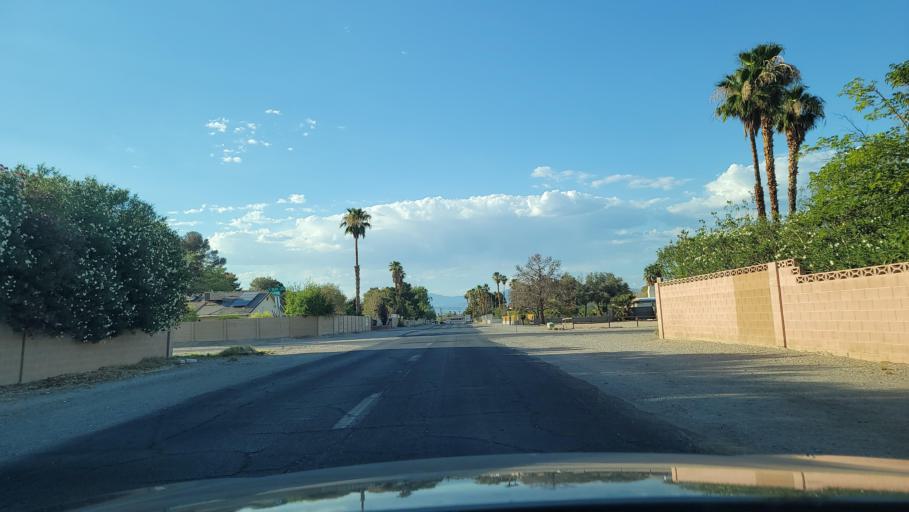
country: US
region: Nevada
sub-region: Clark County
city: Spring Valley
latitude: 36.1532
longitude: -115.2190
